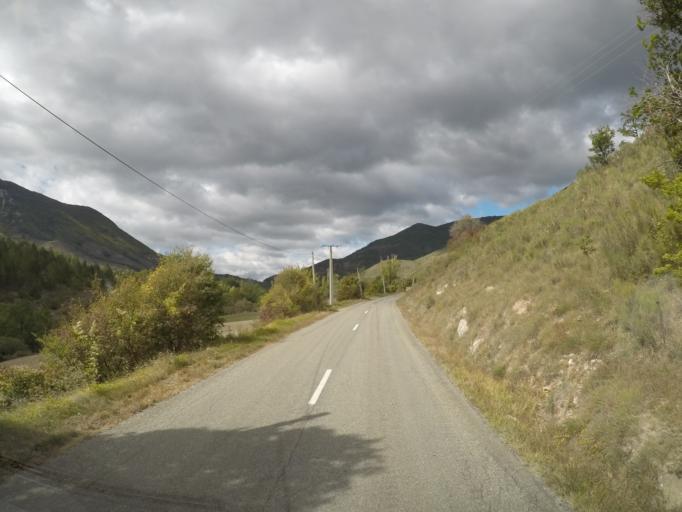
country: FR
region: Provence-Alpes-Cote d'Azur
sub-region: Departement du Vaucluse
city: Sault
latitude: 44.1729
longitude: 5.5944
